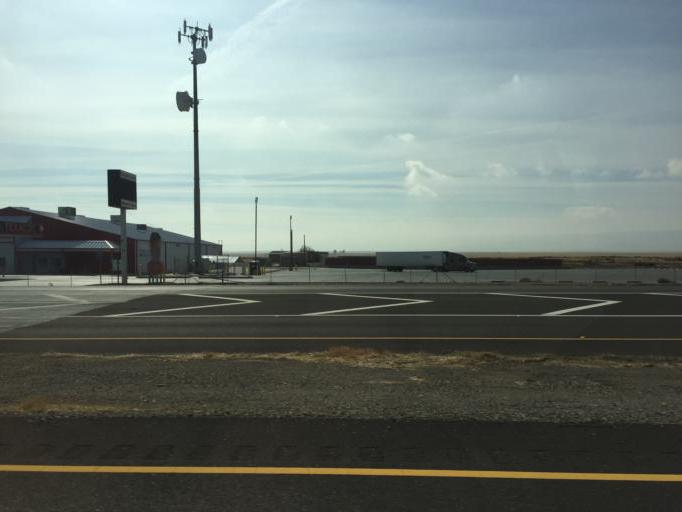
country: US
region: California
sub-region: Kern County
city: Lost Hills
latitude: 35.6152
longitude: -119.8689
